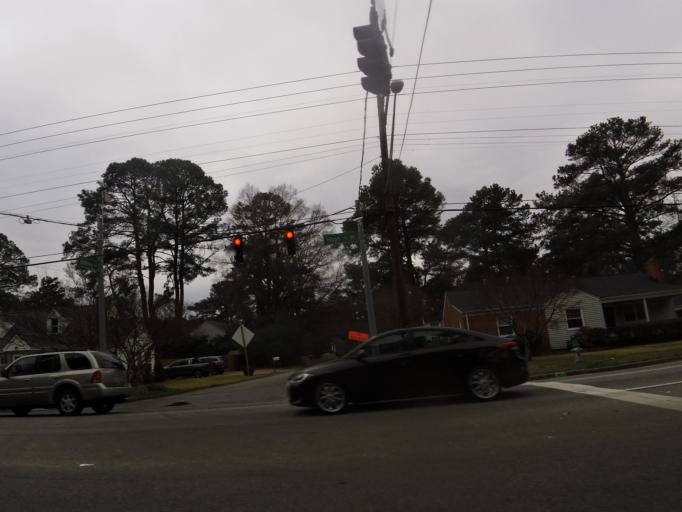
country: US
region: Virginia
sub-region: City of Portsmouth
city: Portsmouth Heights
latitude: 36.8469
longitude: -76.3718
